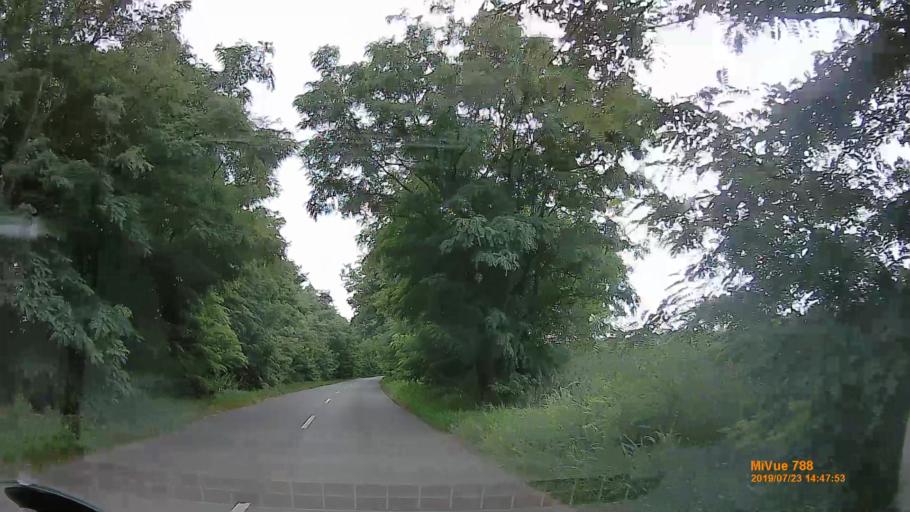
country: HU
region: Szabolcs-Szatmar-Bereg
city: Nyiregyhaza
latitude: 47.9079
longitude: 21.6730
